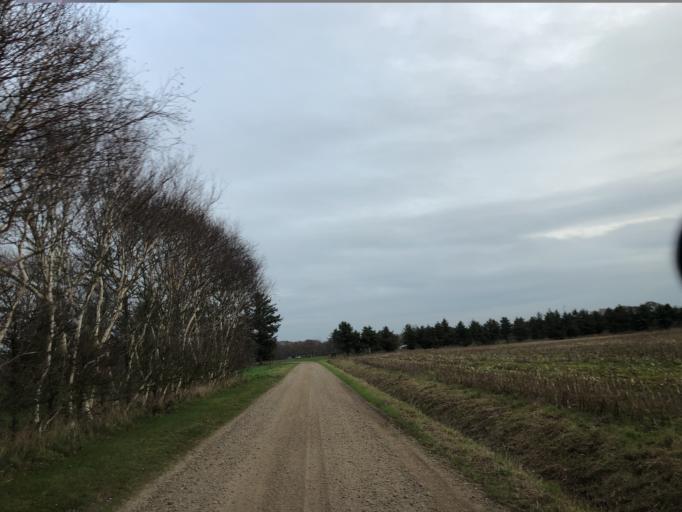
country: DK
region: Central Jutland
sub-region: Holstebro Kommune
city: Ulfborg
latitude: 56.2779
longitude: 8.2279
